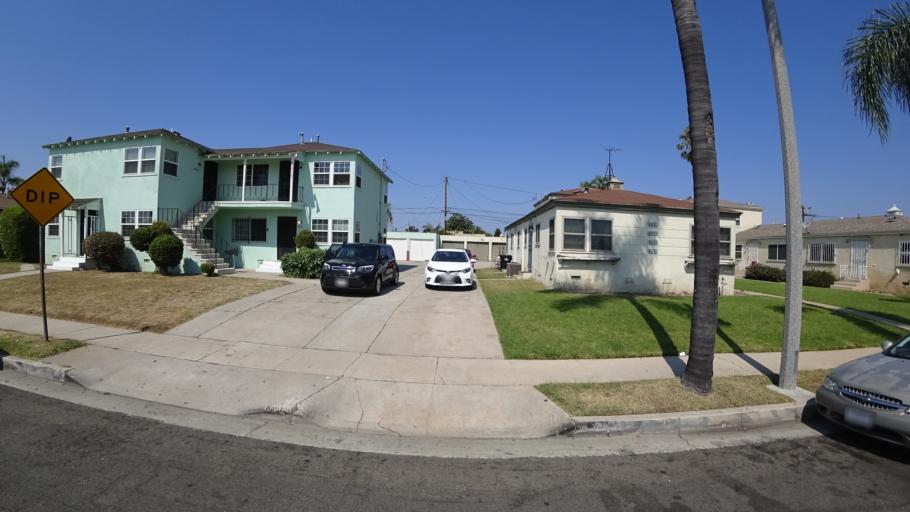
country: US
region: California
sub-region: Los Angeles County
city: Westmont
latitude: 33.9590
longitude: -118.3178
